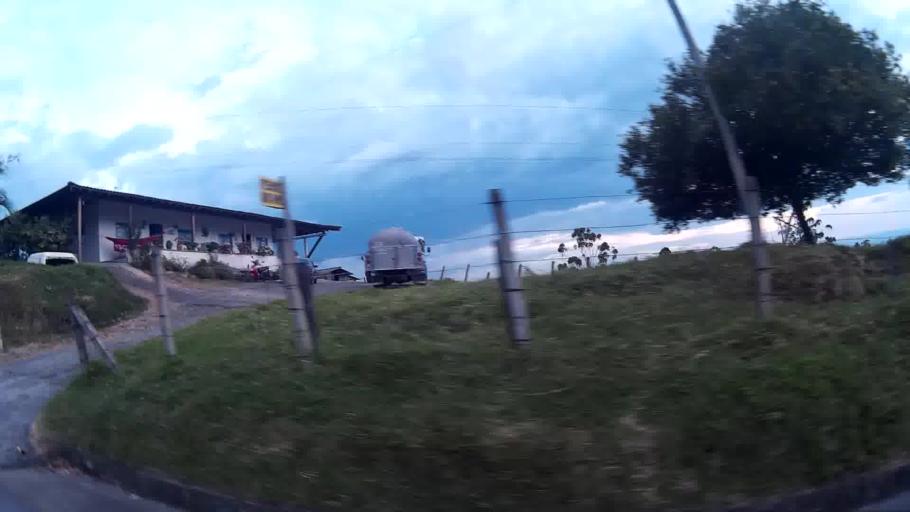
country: CO
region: Quindio
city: Filandia
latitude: 4.7266
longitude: -75.6322
